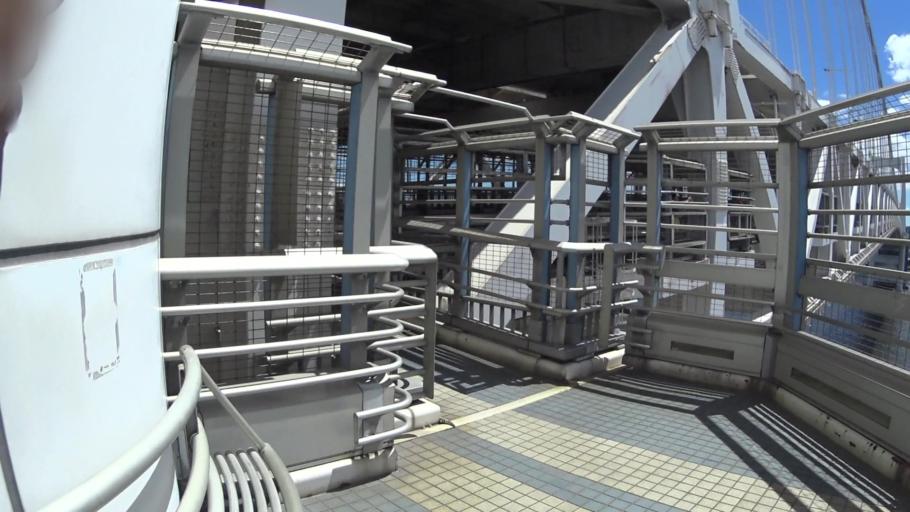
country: JP
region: Tokyo
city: Tokyo
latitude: 35.6346
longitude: 139.7662
